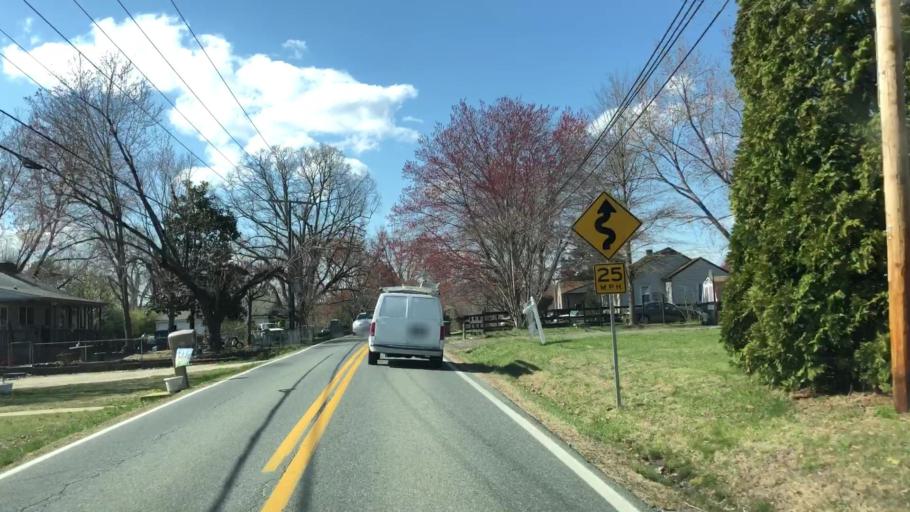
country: US
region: Virginia
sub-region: Stafford County
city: Falmouth
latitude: 38.3481
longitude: -77.4728
